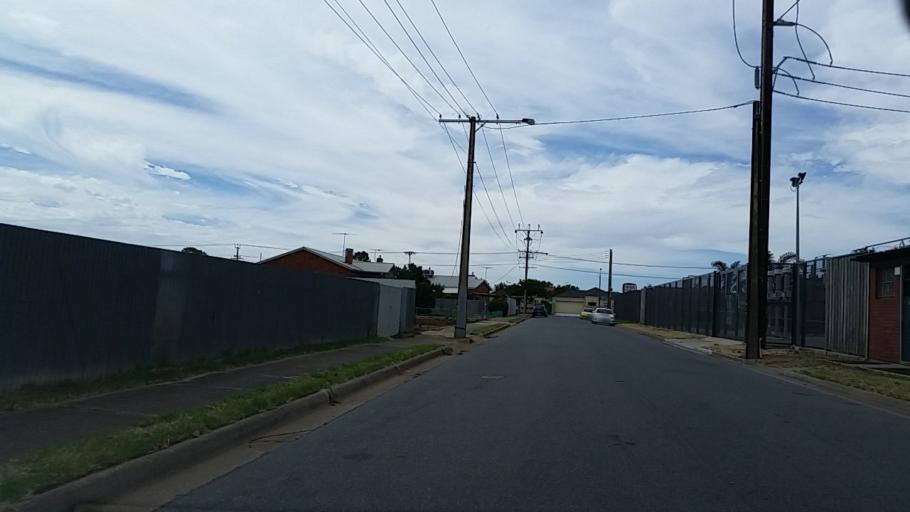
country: AU
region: South Australia
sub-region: Charles Sturt
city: Woodville West
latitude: -34.8922
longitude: 138.5310
